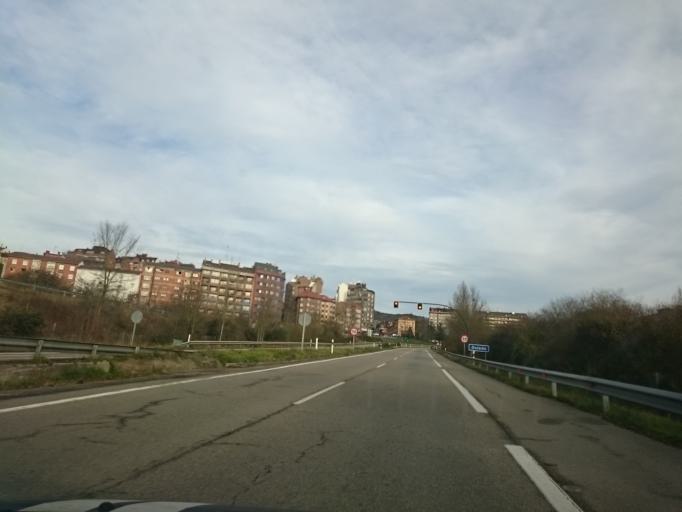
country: ES
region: Asturias
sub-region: Province of Asturias
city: Oviedo
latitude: 43.3515
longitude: -5.8564
